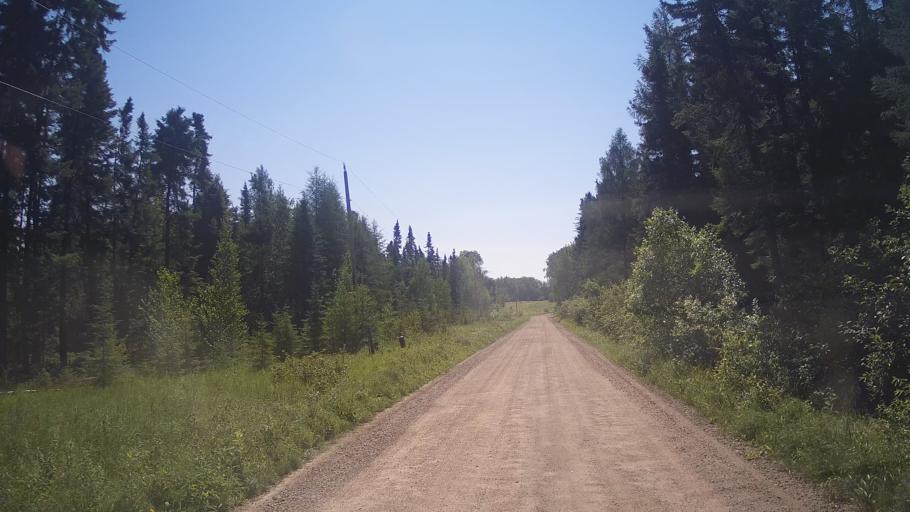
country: CA
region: Ontario
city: Dryden
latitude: 49.8188
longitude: -93.3347
